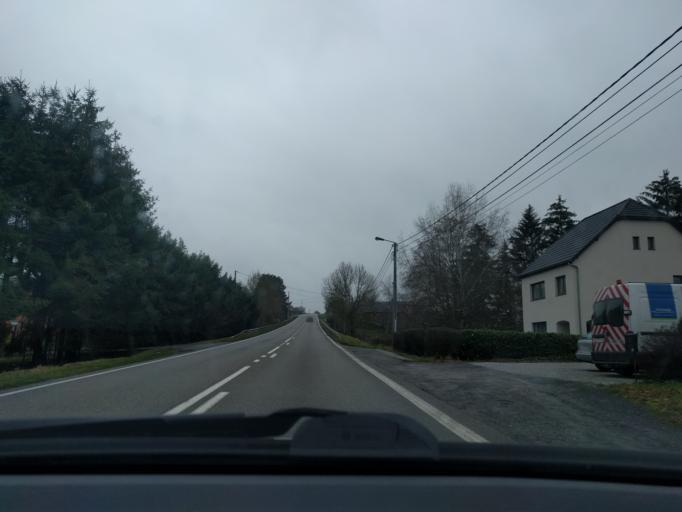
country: BE
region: Wallonia
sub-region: Province de Namur
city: Couvin
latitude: 50.0564
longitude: 4.5234
